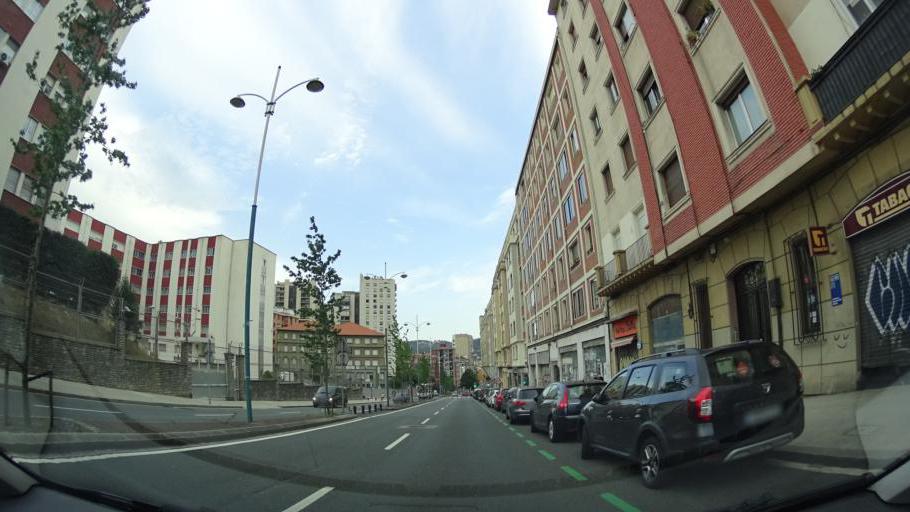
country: ES
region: Basque Country
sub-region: Bizkaia
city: Bilbao
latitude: 43.2540
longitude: -2.9339
